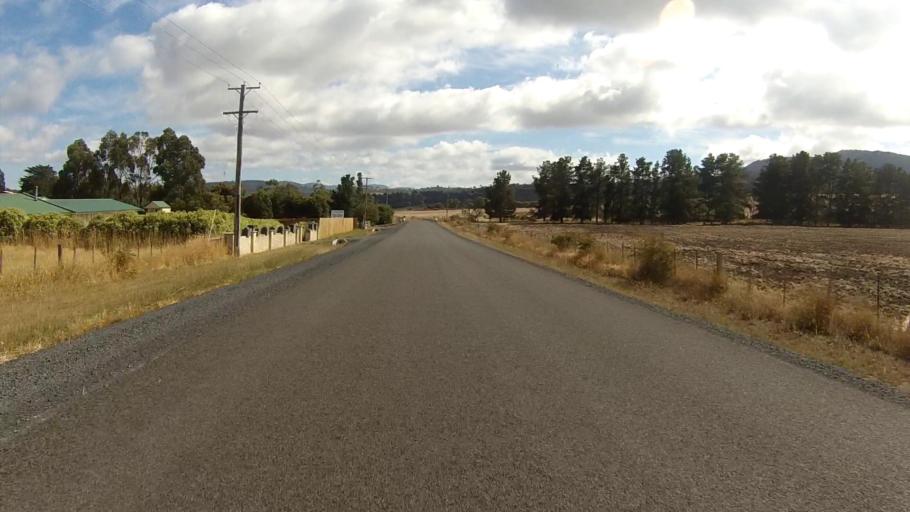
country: AU
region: Tasmania
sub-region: Brighton
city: Old Beach
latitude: -42.7641
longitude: 147.3001
